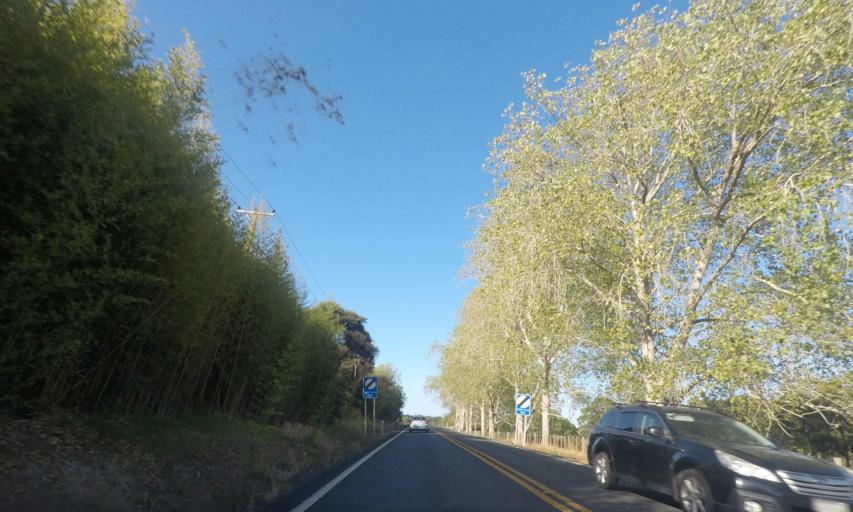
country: NZ
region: Auckland
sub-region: Auckland
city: Muriwai Beach
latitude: -36.7764
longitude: 174.4860
